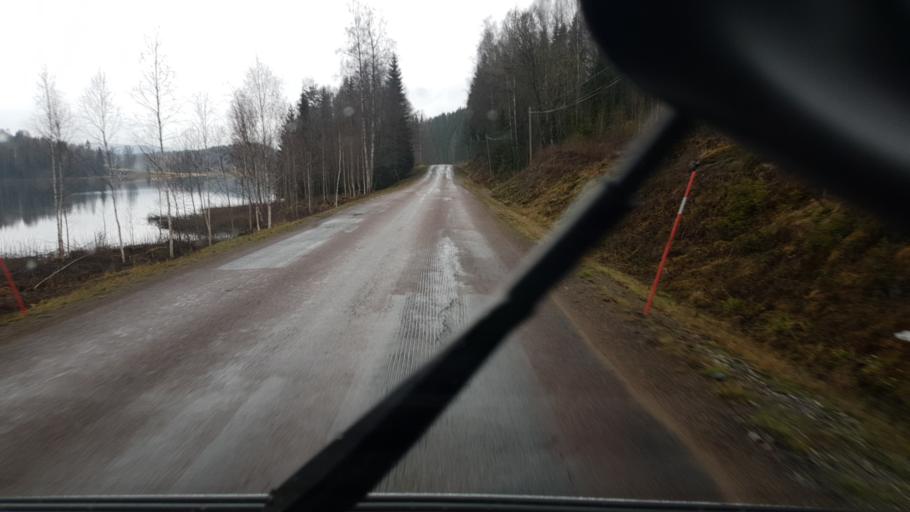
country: SE
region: Vaermland
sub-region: Eda Kommun
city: Amotfors
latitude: 59.8960
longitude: 12.5253
